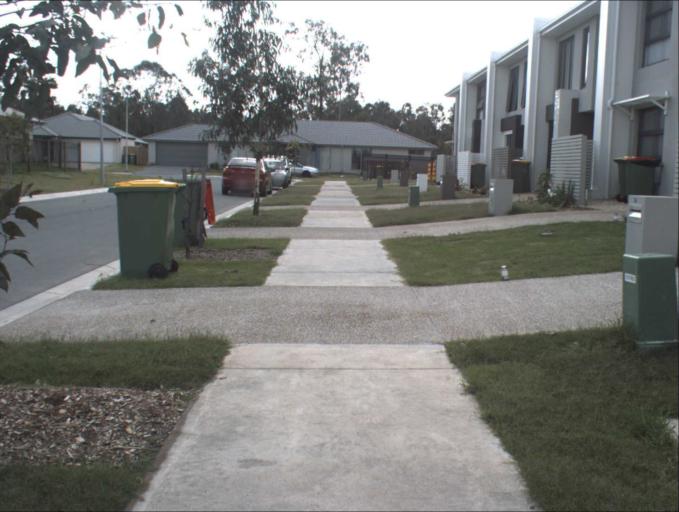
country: AU
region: Queensland
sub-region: Logan
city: Chambers Flat
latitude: -27.7989
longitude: 153.1119
